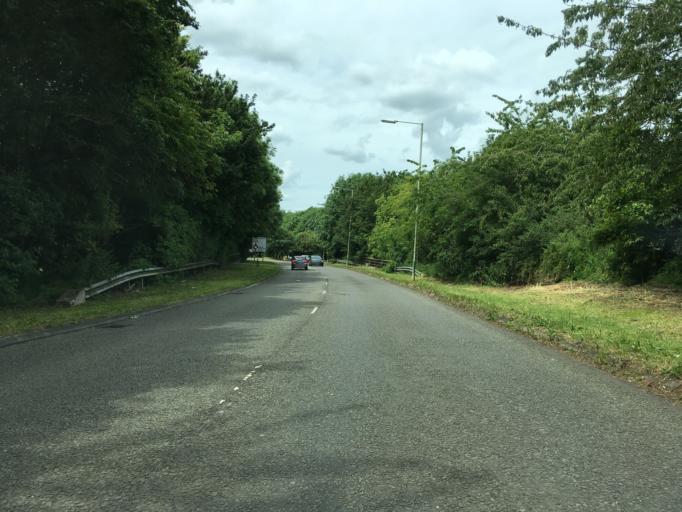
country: GB
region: England
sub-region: Wiltshire
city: Lydiard Tregoze
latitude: 51.5637
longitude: -1.8394
